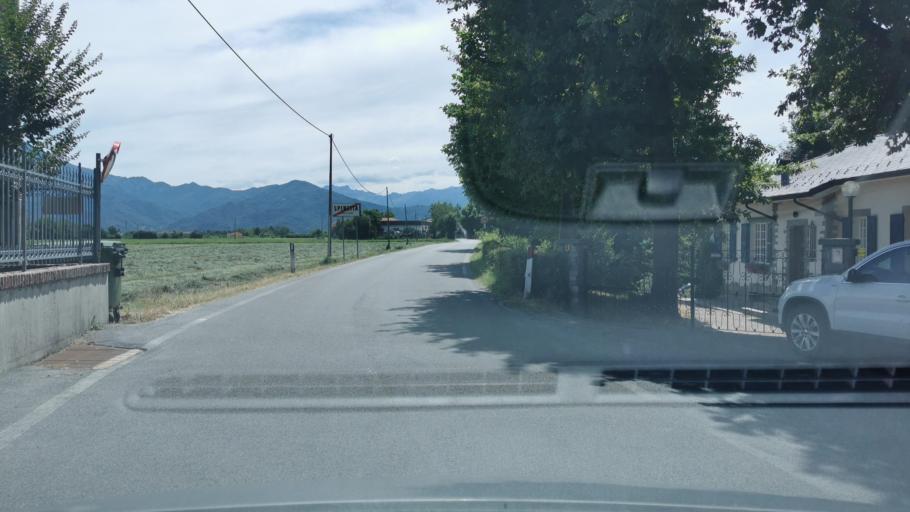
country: IT
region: Piedmont
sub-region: Provincia di Cuneo
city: Cuneo
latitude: 44.3754
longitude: 7.5674
